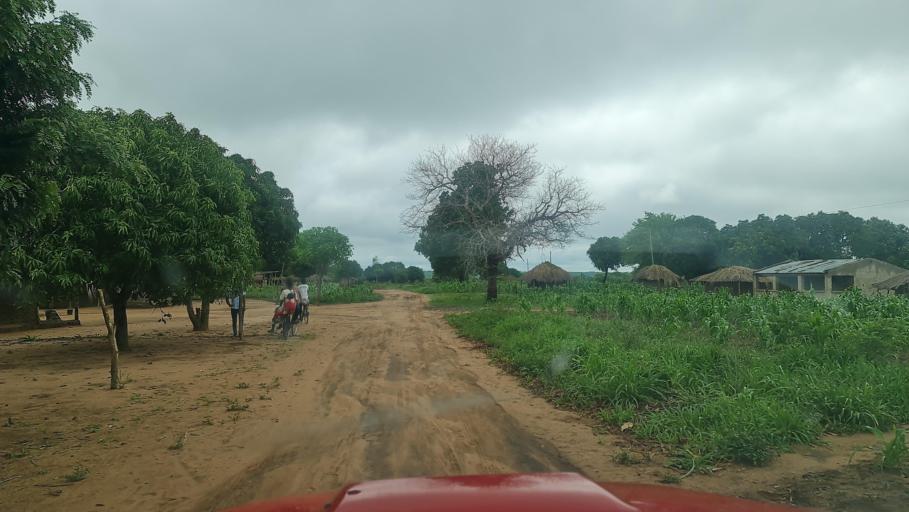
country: MW
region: Southern Region
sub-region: Nsanje District
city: Nsanje
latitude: -17.1947
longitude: 35.8465
